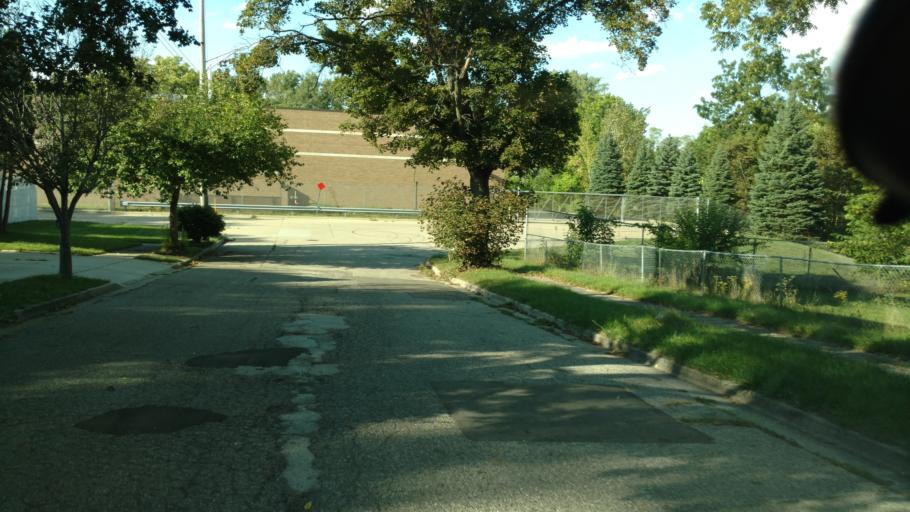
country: US
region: Michigan
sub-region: Ingham County
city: Lansing
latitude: 42.7534
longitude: -84.5656
